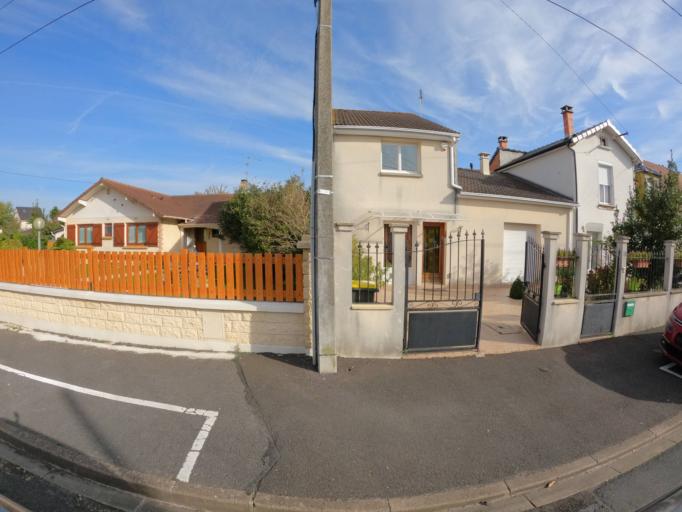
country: FR
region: Ile-de-France
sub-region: Departement de Seine-et-Marne
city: Pontault-Combault
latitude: 48.7902
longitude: 2.6014
